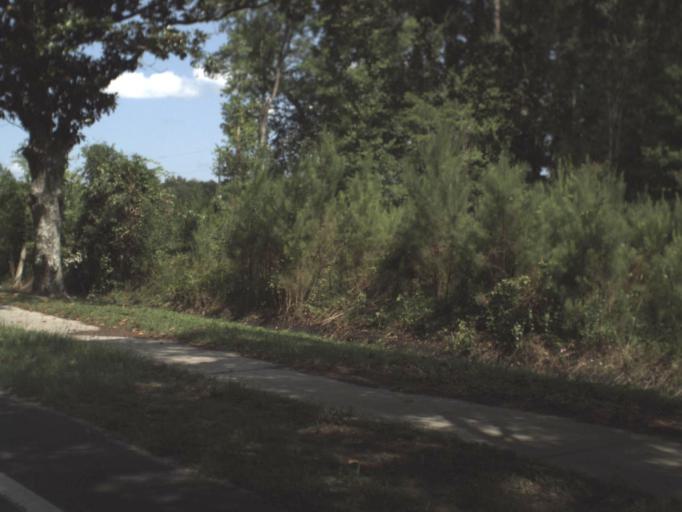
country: US
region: Florida
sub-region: Clay County
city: Asbury Lake
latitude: 29.9826
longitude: -81.7984
